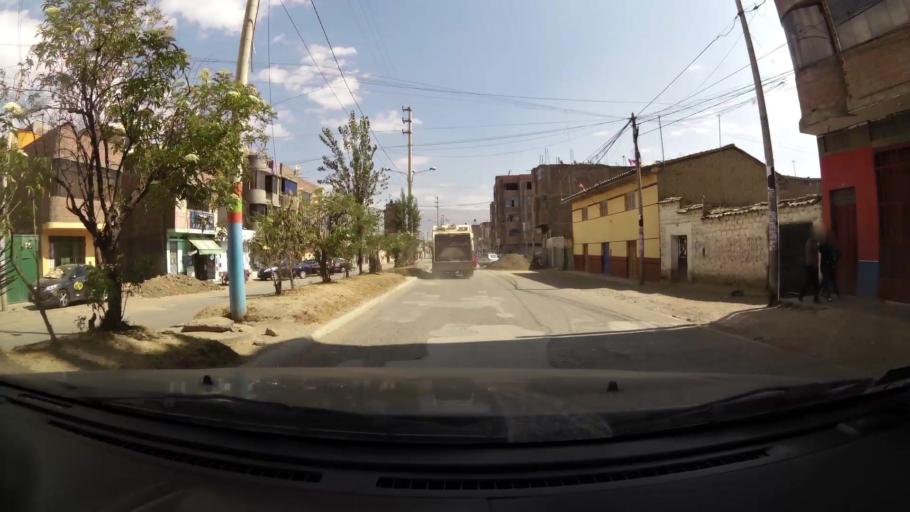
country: PE
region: Junin
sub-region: Provincia de Huancayo
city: Huancayo
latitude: -12.0878
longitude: -75.2025
